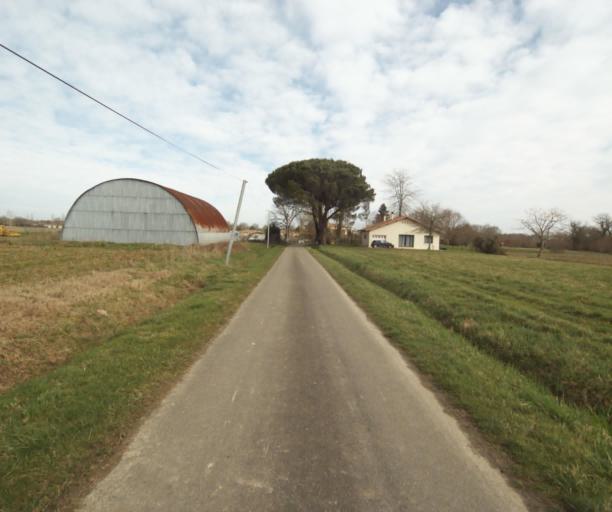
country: FR
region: Aquitaine
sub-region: Departement des Landes
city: Gabarret
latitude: 43.9816
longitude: 0.0023
